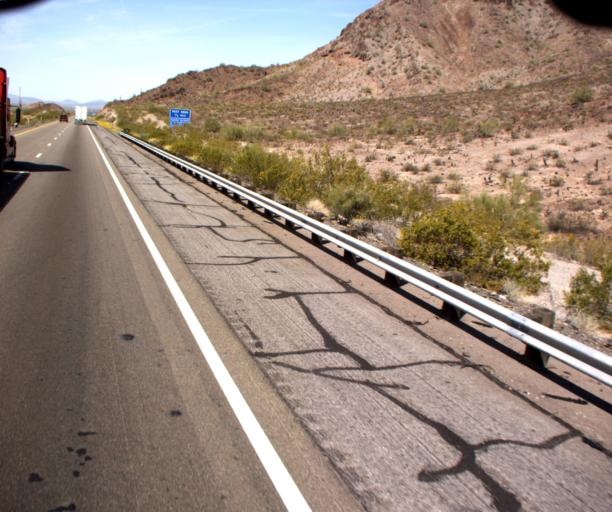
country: US
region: Arizona
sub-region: La Paz County
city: Salome
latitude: 33.6112
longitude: -113.6324
